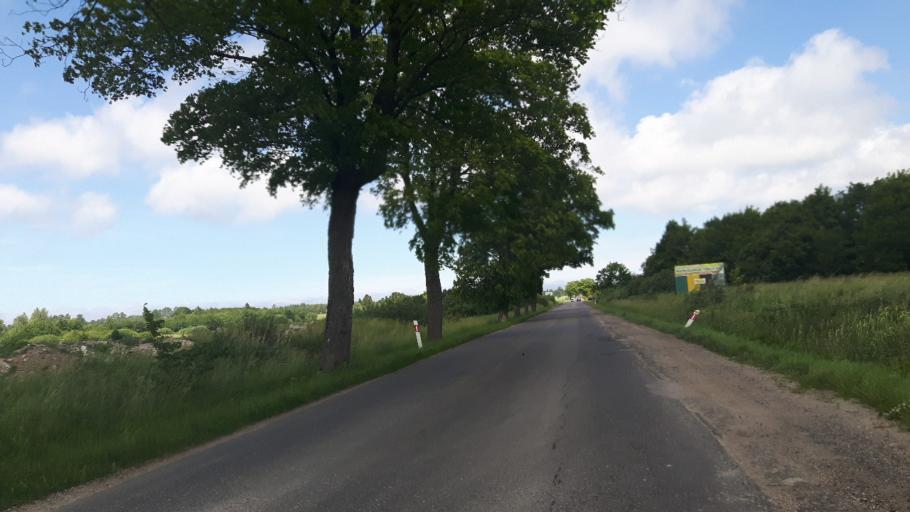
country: PL
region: Pomeranian Voivodeship
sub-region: Powiat slupski
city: Ustka
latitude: 54.5509
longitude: 16.8347
